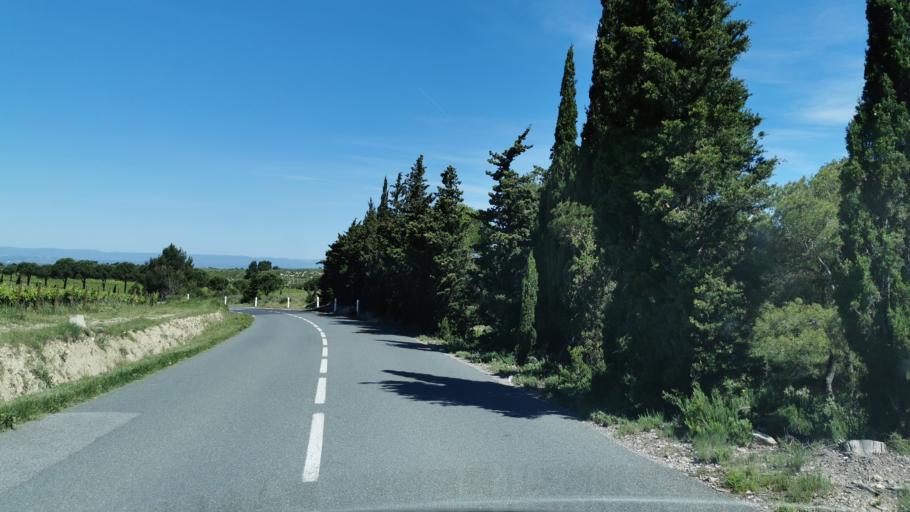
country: FR
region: Languedoc-Roussillon
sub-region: Departement de l'Aude
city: Armissan
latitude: 43.1740
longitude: 3.1116
